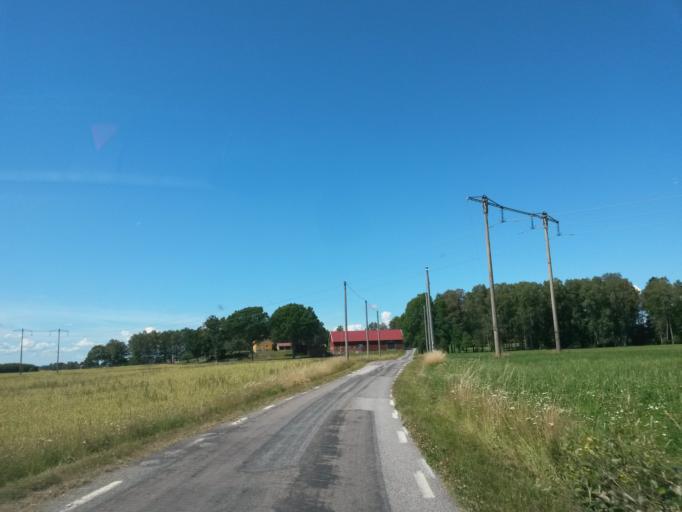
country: SE
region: Vaestra Goetaland
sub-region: Grastorps Kommun
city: Graestorp
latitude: 58.3809
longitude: 12.7653
